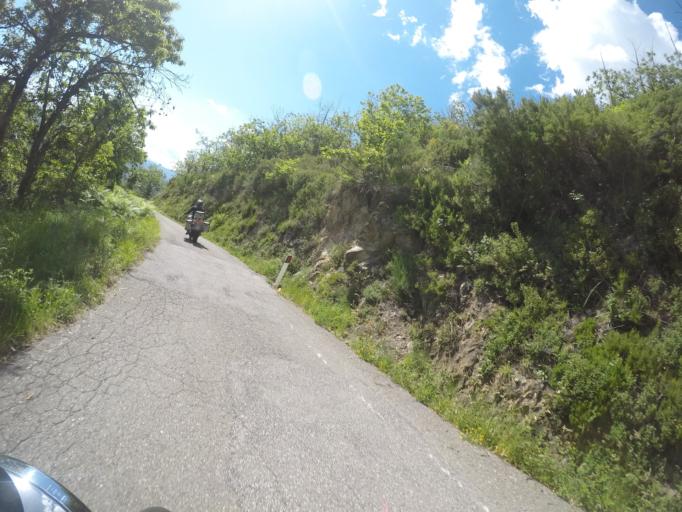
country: IT
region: Tuscany
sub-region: Provincia di Massa-Carrara
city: Casola in Lunigiana
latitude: 44.1790
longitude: 10.1693
